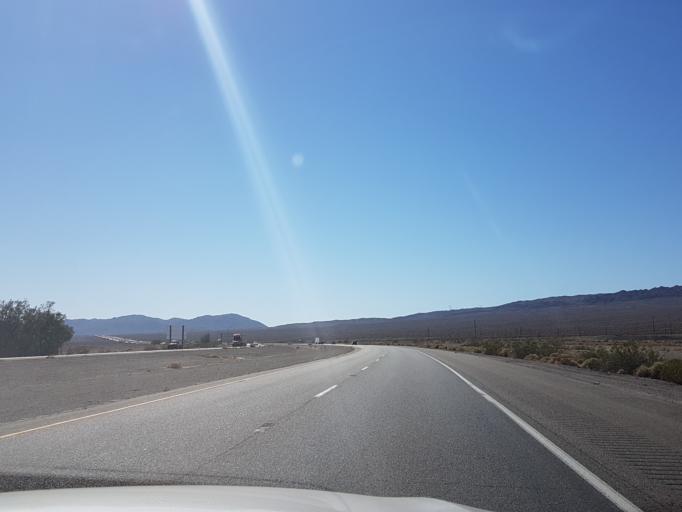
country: US
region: California
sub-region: San Bernardino County
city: Fort Irwin
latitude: 35.2551
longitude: -116.0867
